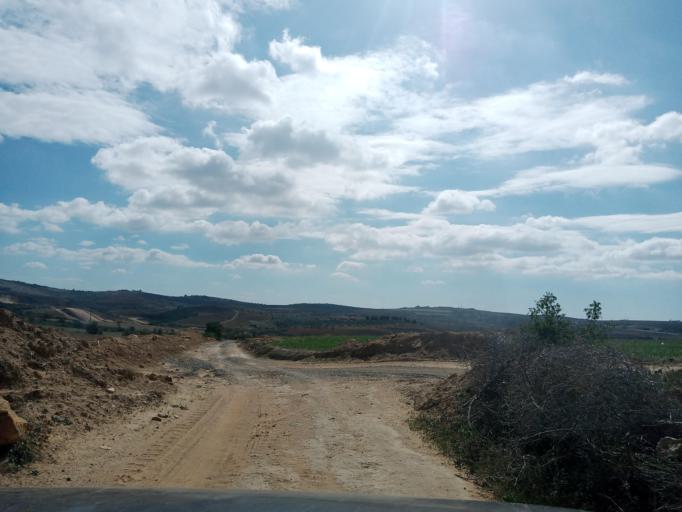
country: TN
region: Tunis
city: Oued Lill
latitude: 36.8077
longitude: 9.9852
